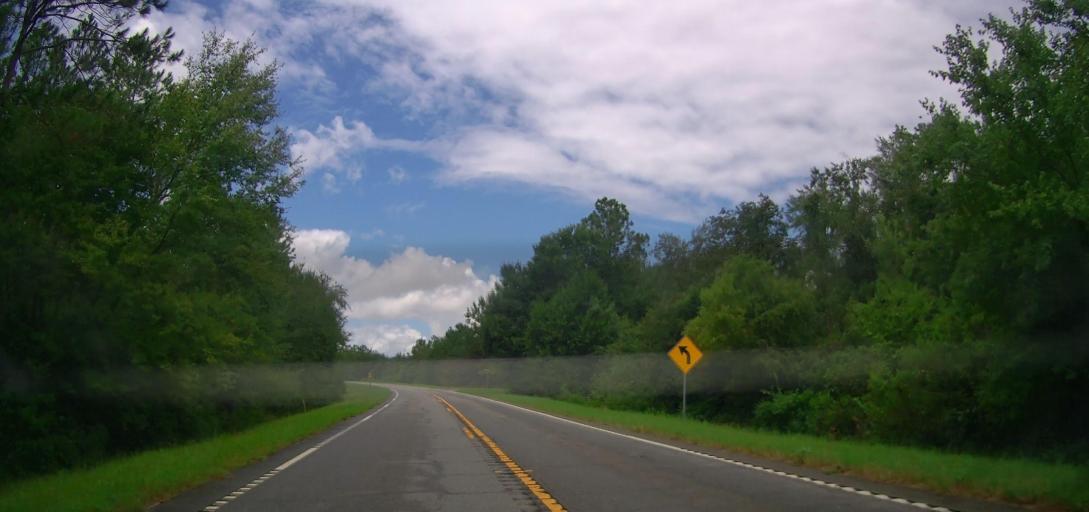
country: US
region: Georgia
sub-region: Crisp County
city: Cordele
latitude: 32.0428
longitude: -83.6193
